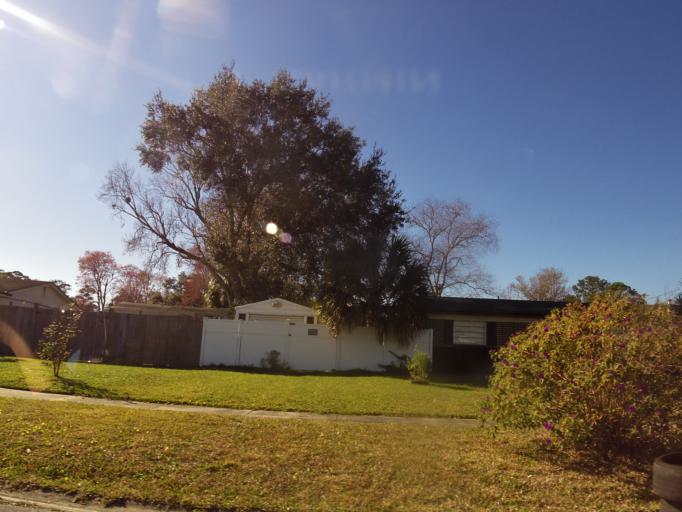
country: US
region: Florida
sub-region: Duval County
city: Jacksonville
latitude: 30.2675
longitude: -81.6034
